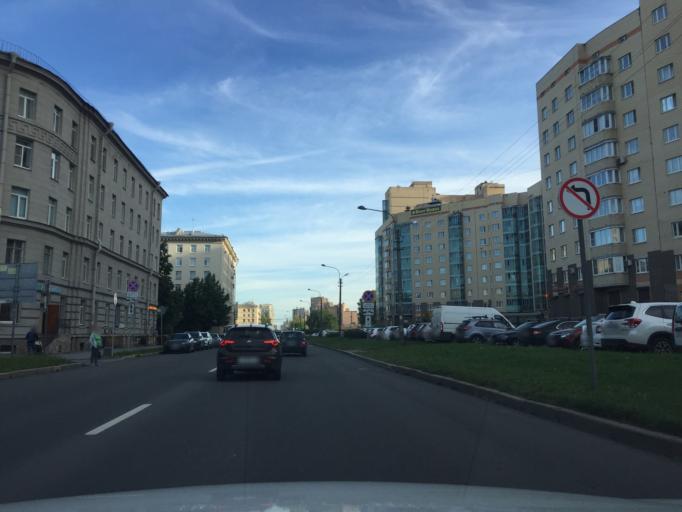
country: RU
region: St.-Petersburg
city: Kupchino
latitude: 59.8680
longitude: 30.3138
